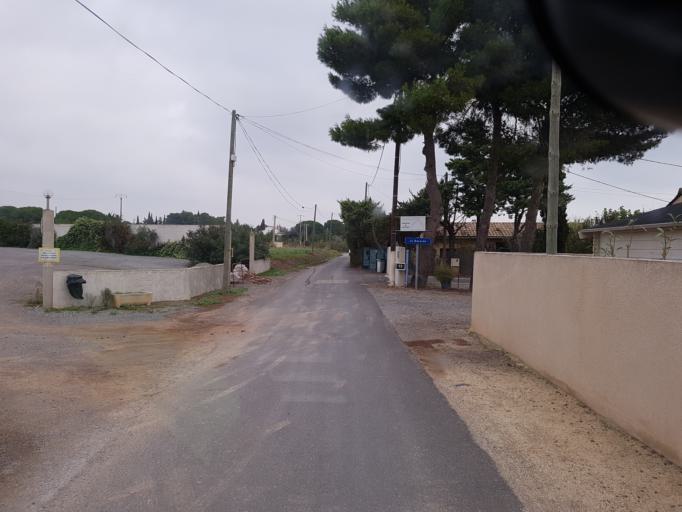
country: FR
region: Languedoc-Roussillon
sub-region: Departement de l'Herault
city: Marseillan
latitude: 43.3668
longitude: 3.5388
